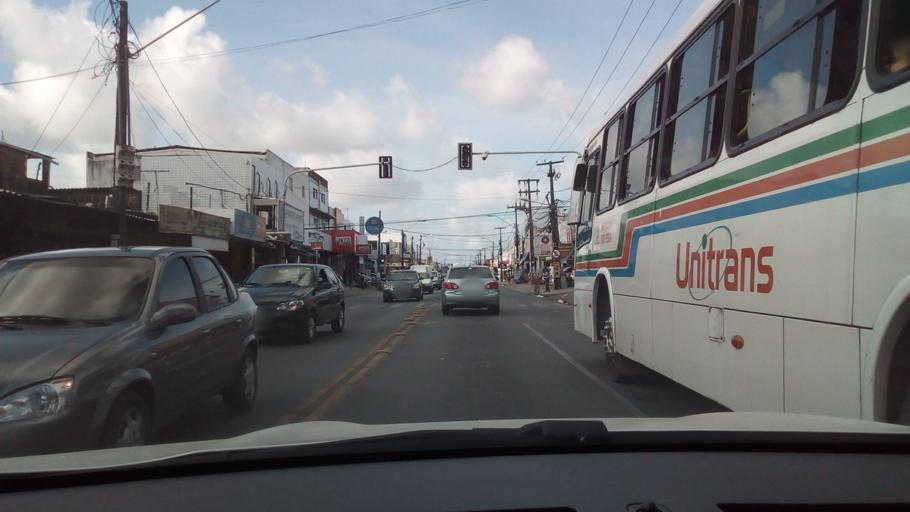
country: BR
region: Paraiba
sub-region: Joao Pessoa
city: Joao Pessoa
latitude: -7.1667
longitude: -34.8385
